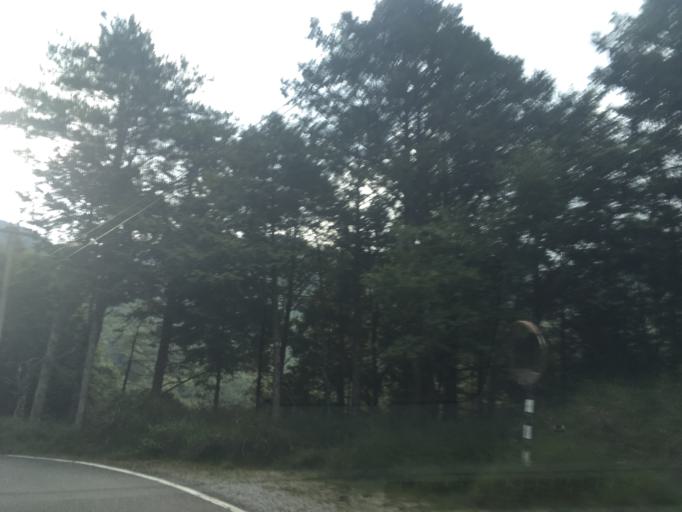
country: TW
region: Taiwan
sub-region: Nantou
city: Puli
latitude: 24.2613
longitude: 121.0165
